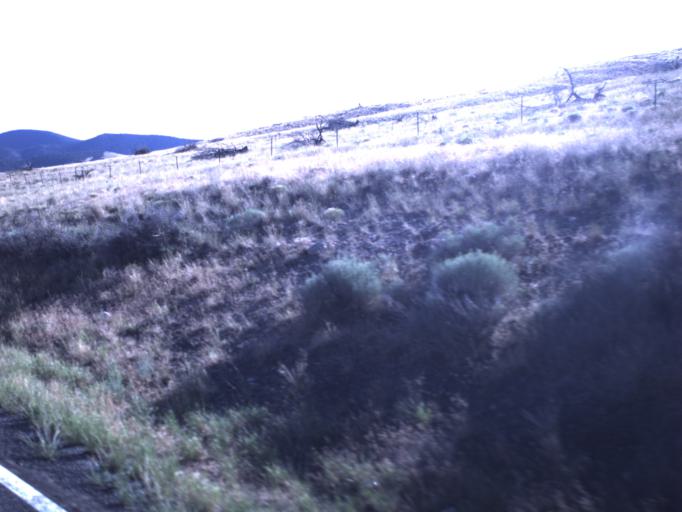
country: US
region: Utah
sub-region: Iron County
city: Parowan
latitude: 38.0820
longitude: -112.9570
